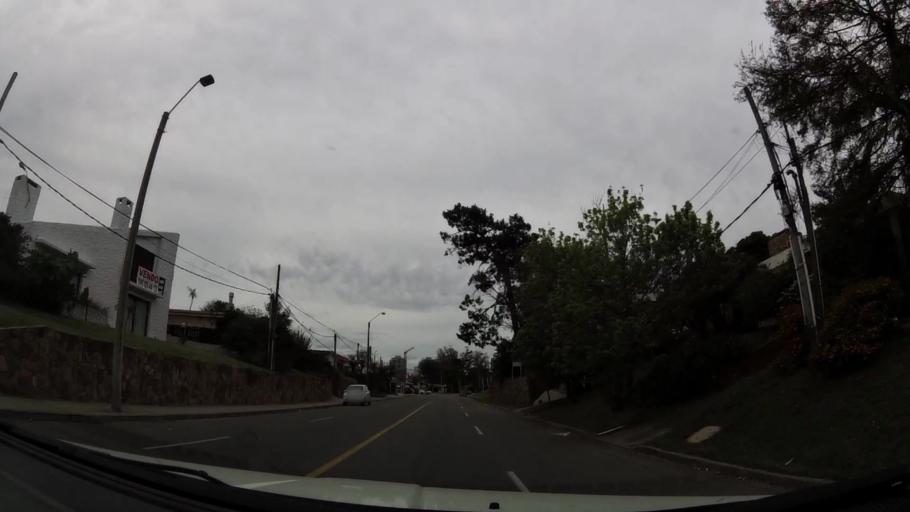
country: UY
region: Maldonado
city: Maldonado
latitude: -34.9186
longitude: -54.9613
